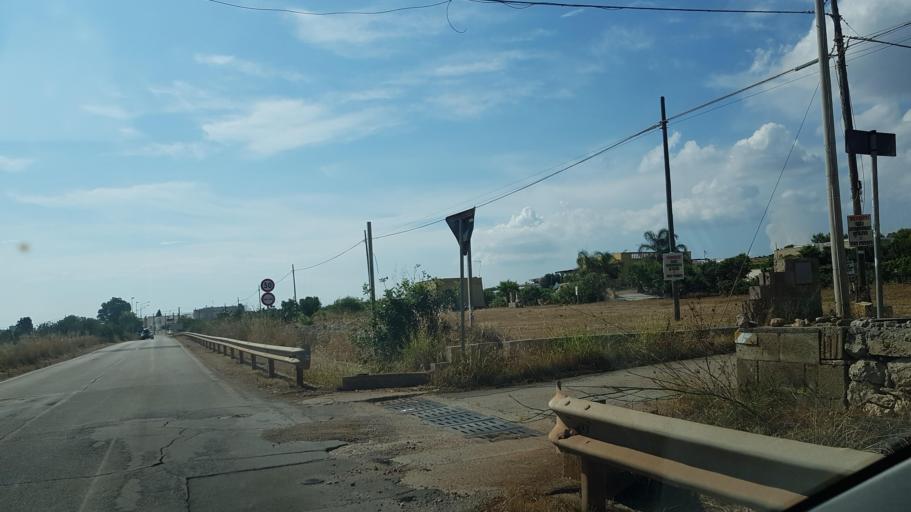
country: IT
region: Apulia
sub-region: Provincia di Lecce
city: Acquarica del Capo
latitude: 39.8431
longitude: 18.2157
